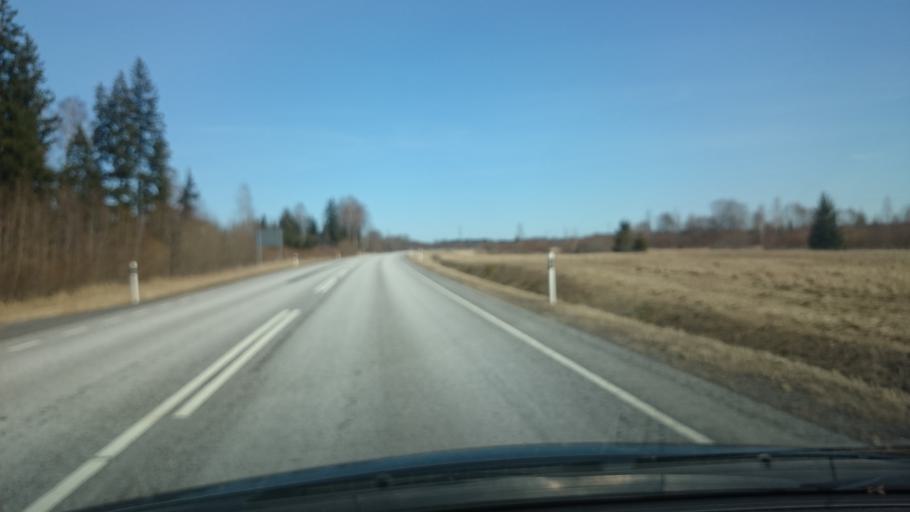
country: EE
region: Paernumaa
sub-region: Vaendra vald (alev)
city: Vandra
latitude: 58.6552
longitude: 25.0026
